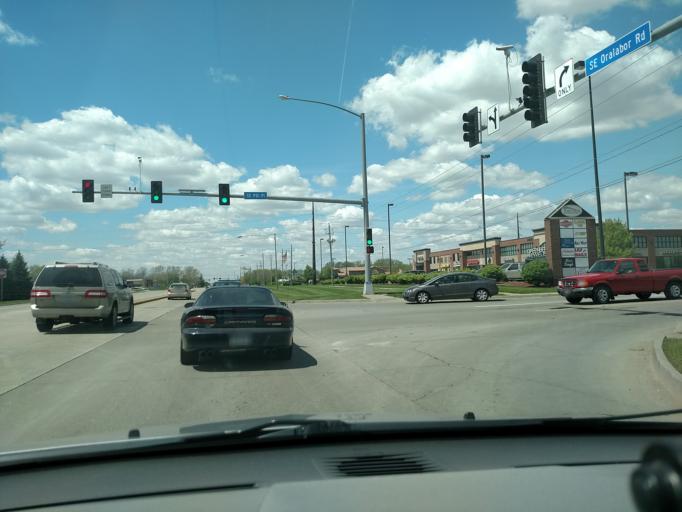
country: US
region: Iowa
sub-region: Polk County
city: Ankeny
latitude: 41.7029
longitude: -93.5842
